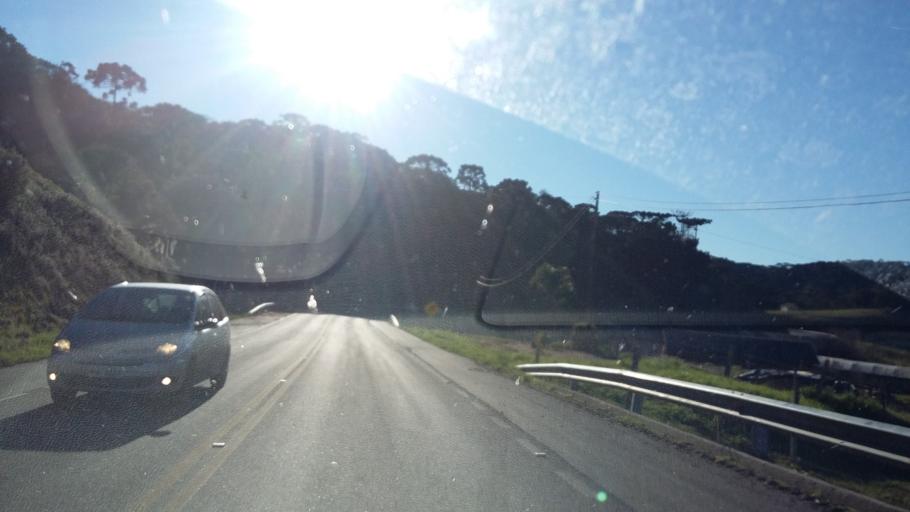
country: BR
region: Santa Catarina
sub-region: Lauro Muller
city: Lauro Muller
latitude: -28.0106
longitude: -49.5345
